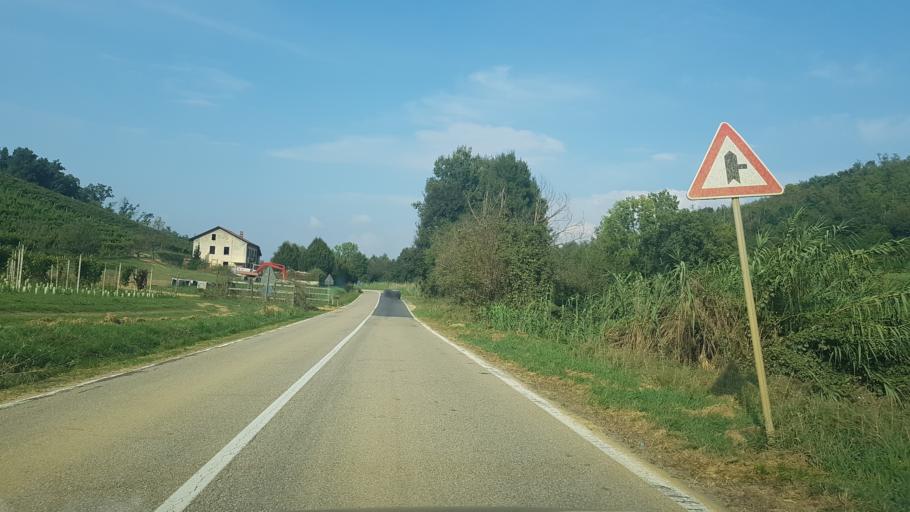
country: IT
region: Piedmont
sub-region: Provincia di Asti
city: Castelnuovo Belbo
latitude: 44.7917
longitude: 8.4238
